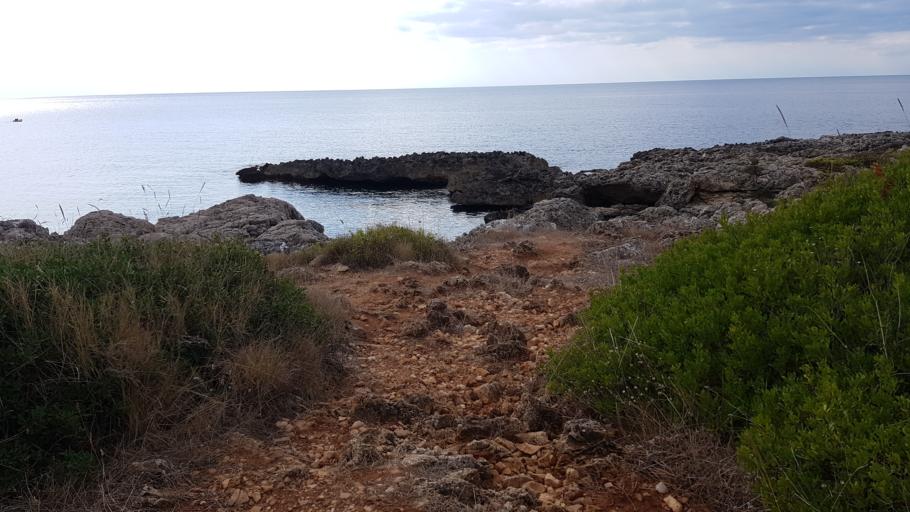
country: IT
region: Apulia
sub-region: Provincia di Lecce
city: Nardo
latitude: 40.1632
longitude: 17.9520
